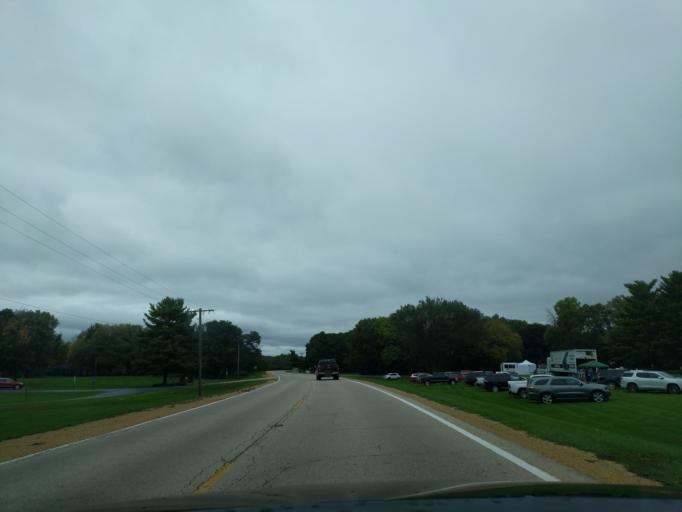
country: US
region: Illinois
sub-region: Ogle County
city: Oregon
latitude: 42.0169
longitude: -89.3243
